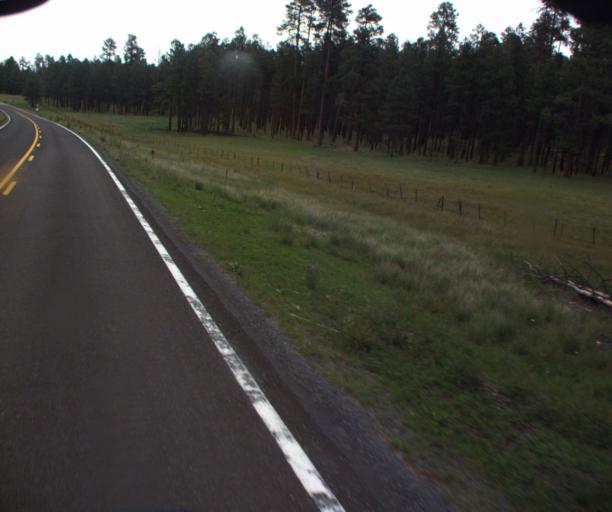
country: US
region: Arizona
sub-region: Apache County
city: Eagar
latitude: 33.6871
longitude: -109.2215
